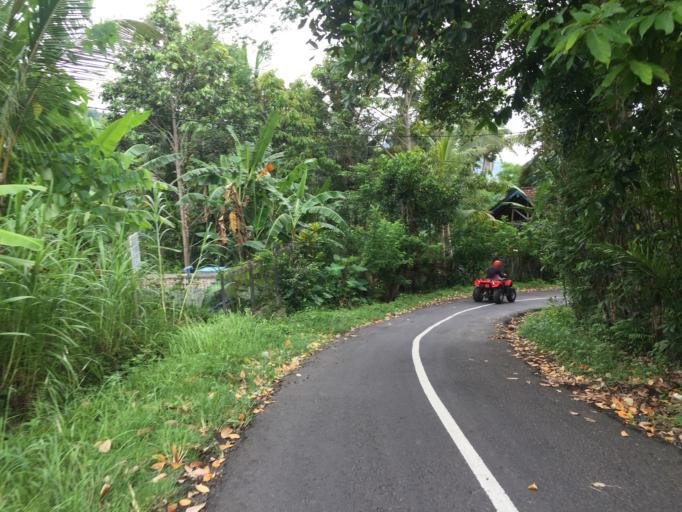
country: ID
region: Bali
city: Banjar Kawan
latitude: -8.4717
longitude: 115.5182
